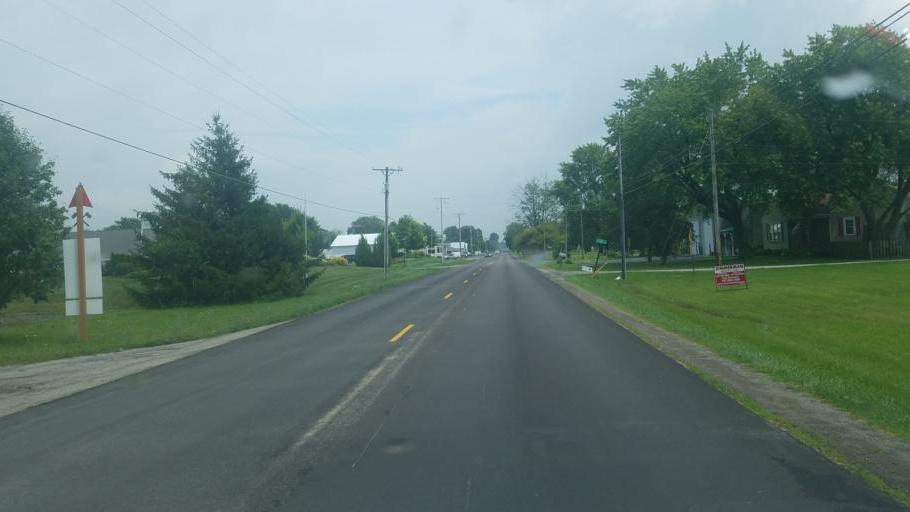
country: US
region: Ohio
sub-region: Logan County
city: Russells Point
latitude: 40.4688
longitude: -83.8678
